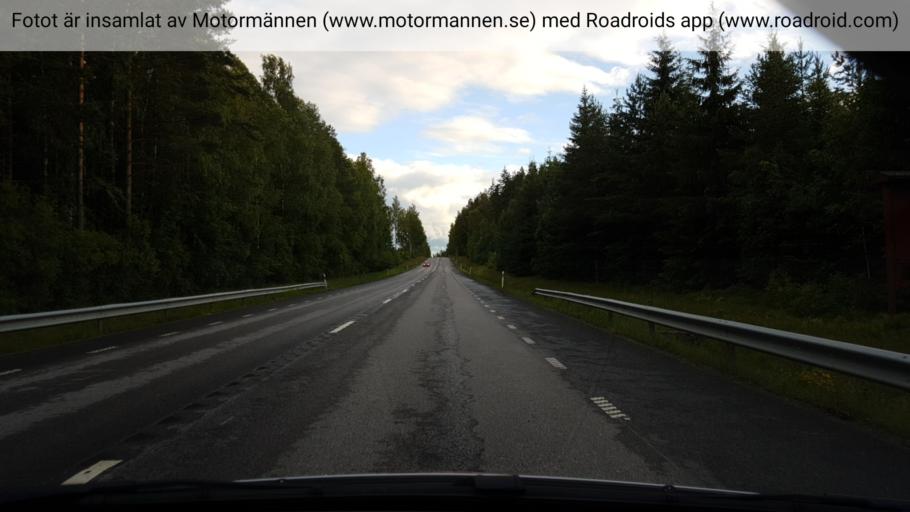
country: SE
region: OErebro
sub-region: Hallefors Kommun
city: Haellefors
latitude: 59.7606
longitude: 14.5163
